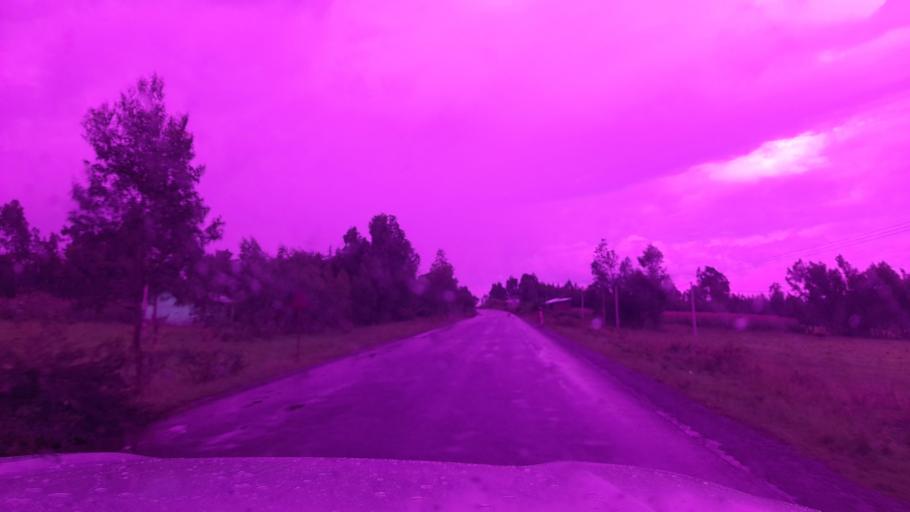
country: ET
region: Oromiya
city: Jima
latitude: 7.7071
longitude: 37.0728
